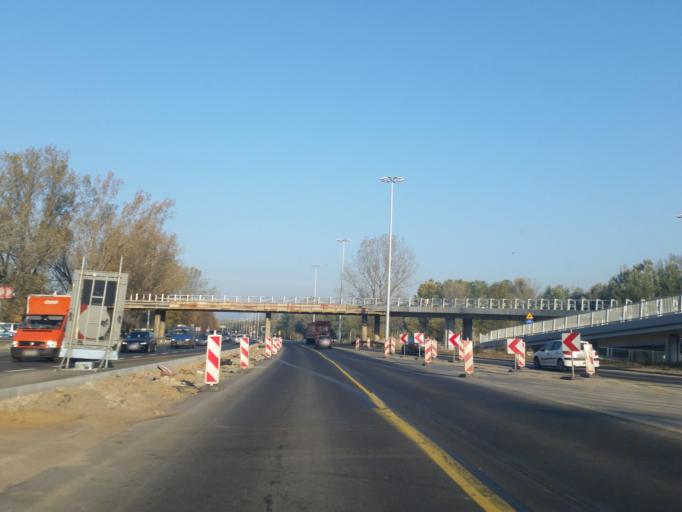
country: PL
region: Masovian Voivodeship
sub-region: Warszawa
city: Zoliborz
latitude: 52.2846
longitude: 20.9882
